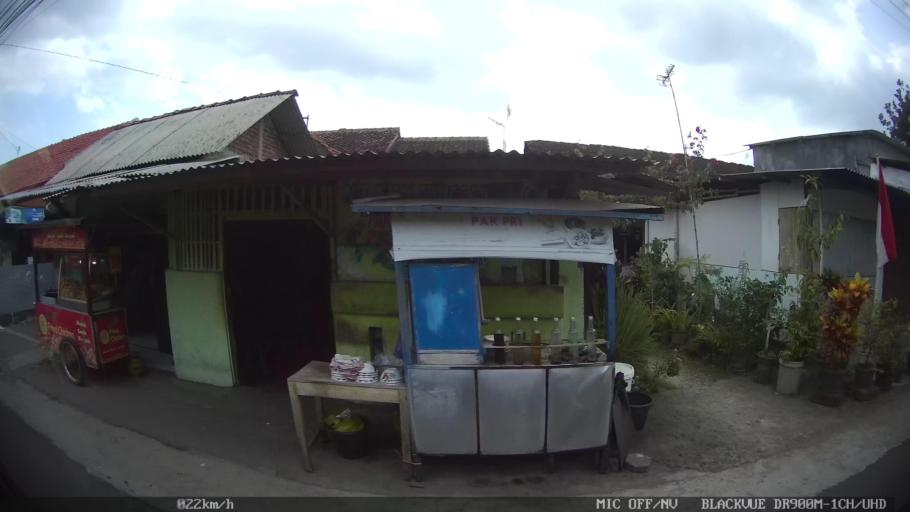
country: ID
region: Daerah Istimewa Yogyakarta
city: Yogyakarta
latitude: -7.7697
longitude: 110.3386
